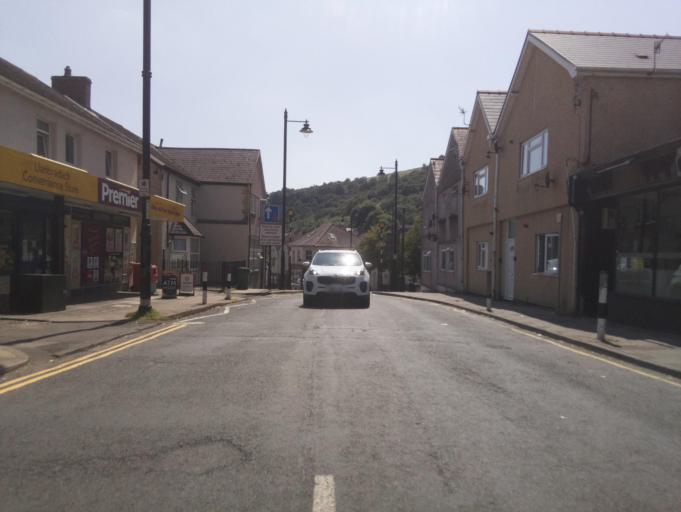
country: GB
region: Wales
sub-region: Caerphilly County Borough
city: Llanbradach
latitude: 51.6047
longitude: -3.2308
